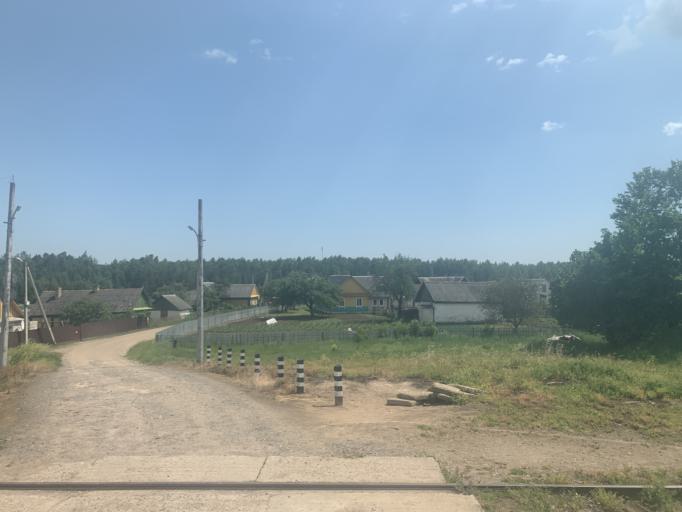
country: BY
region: Minsk
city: Stowbtsy
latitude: 53.4946
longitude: 26.7744
